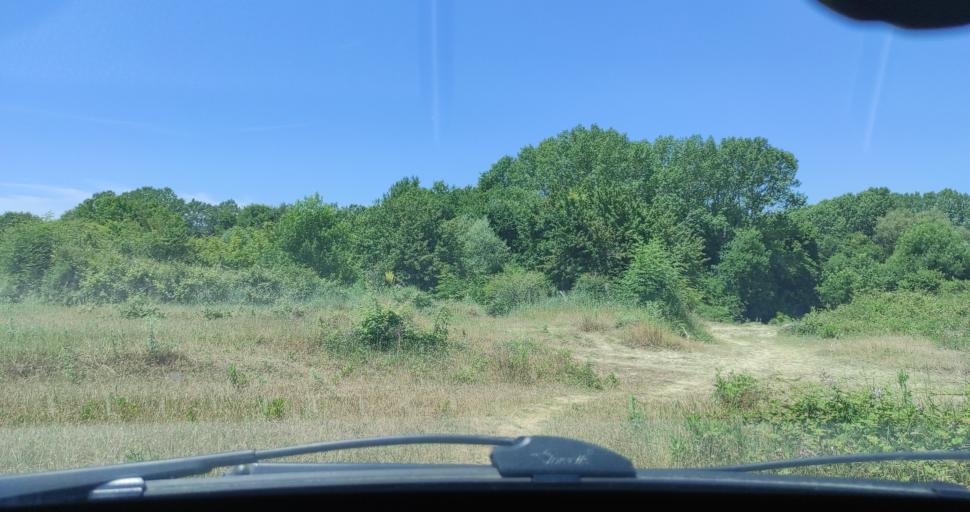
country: AL
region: Shkoder
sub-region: Rrethi i Shkodres
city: Velipoje
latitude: 41.8846
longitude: 19.3849
